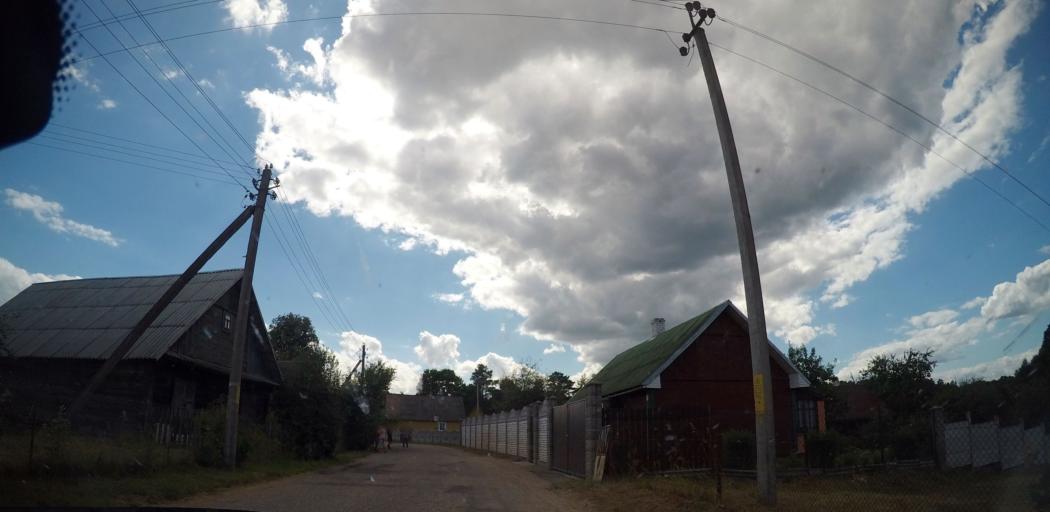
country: BY
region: Grodnenskaya
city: Skidal'
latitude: 53.8199
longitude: 24.2453
